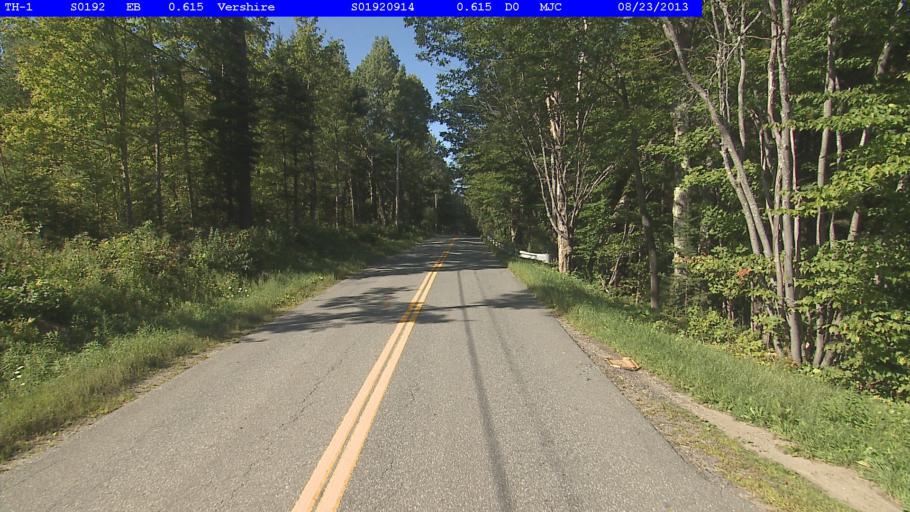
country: US
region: Vermont
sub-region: Orange County
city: Chelsea
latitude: 43.9957
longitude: -72.3656
